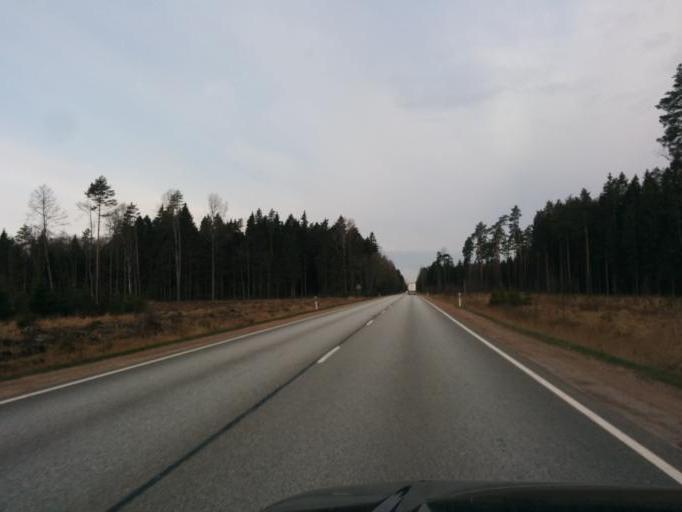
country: LV
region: Kekava
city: Kekava
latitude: 56.8118
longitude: 24.1605
